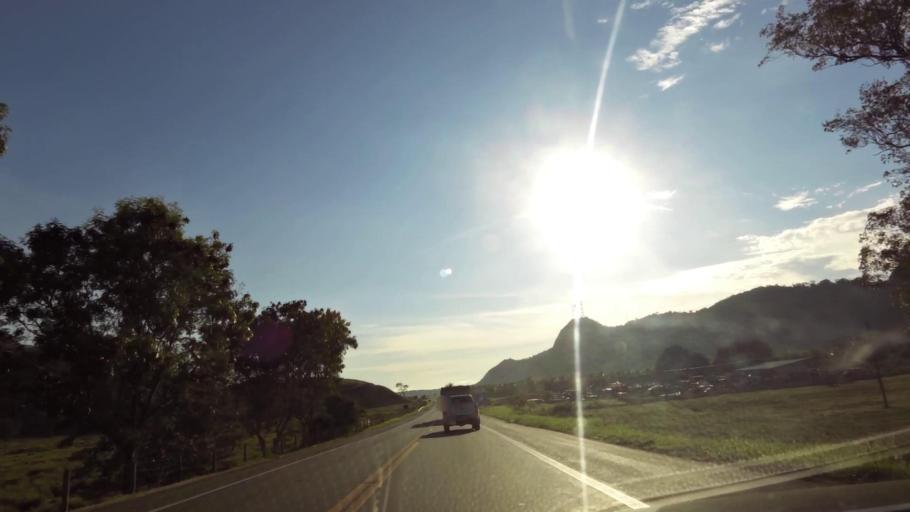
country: BR
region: Espirito Santo
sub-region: Guarapari
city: Guarapari
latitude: -20.6229
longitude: -40.5223
